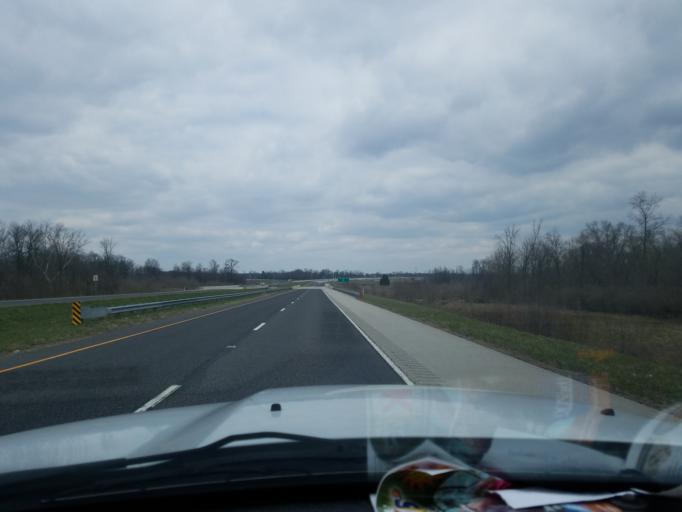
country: US
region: Indiana
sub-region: Vigo County
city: Terre Haute
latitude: 39.3896
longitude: -87.3728
